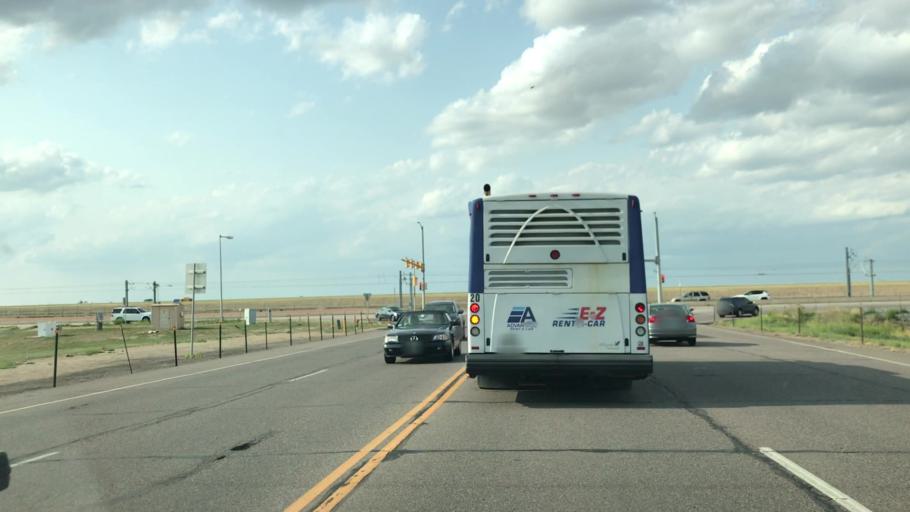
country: US
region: Colorado
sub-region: Weld County
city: Lochbuie
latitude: 39.8370
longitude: -104.6929
